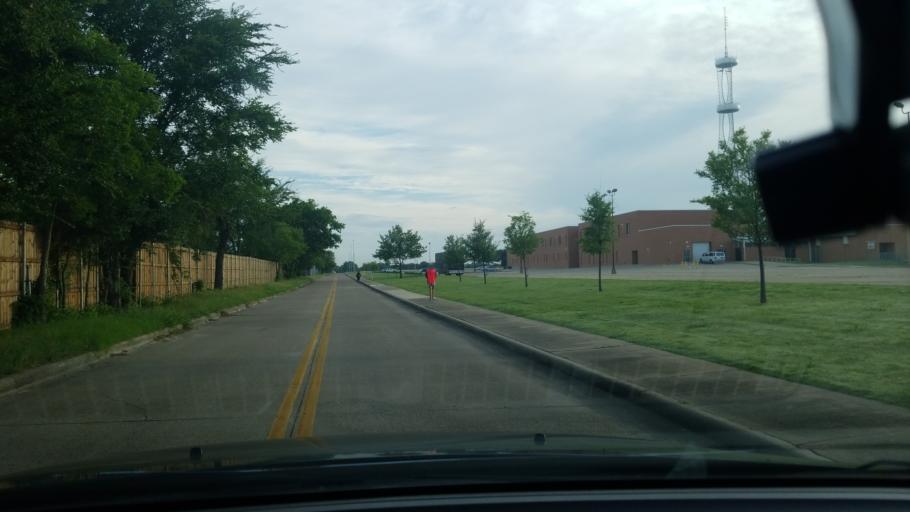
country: US
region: Texas
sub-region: Dallas County
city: Balch Springs
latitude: 32.7592
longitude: -96.6372
